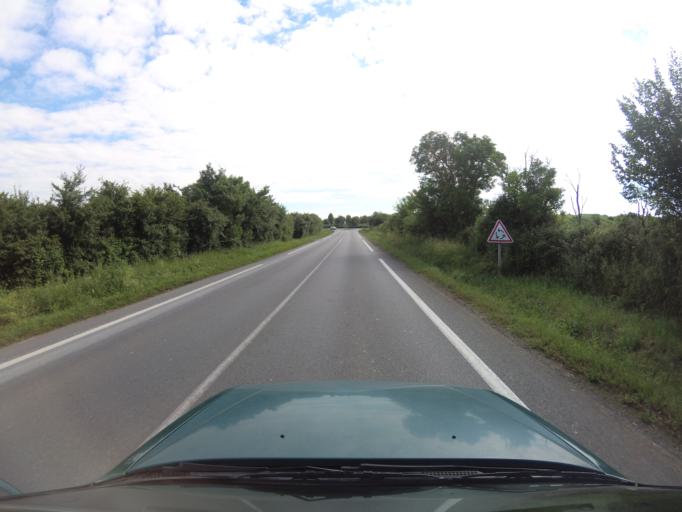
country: FR
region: Poitou-Charentes
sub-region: Departement de la Charente-Maritime
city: Saint-Xandre
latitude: 46.2183
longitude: -1.0886
